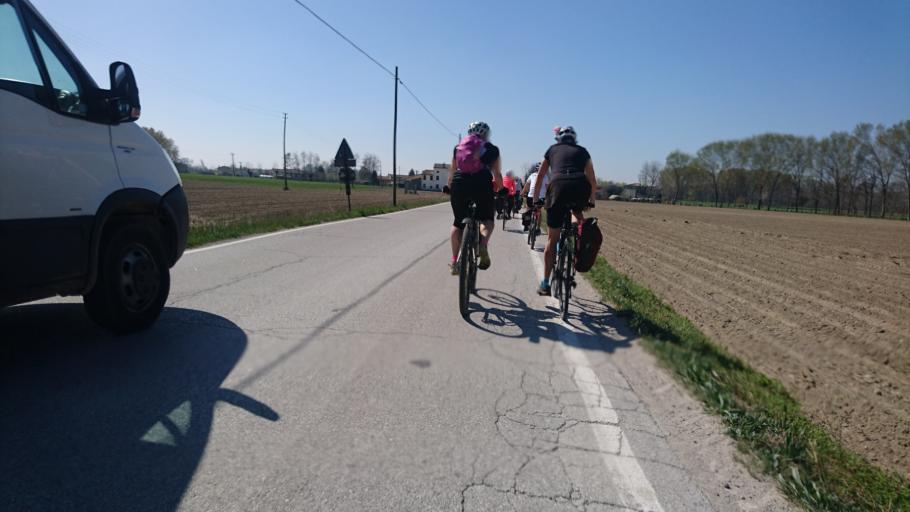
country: IT
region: Veneto
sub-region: Provincia di Padova
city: San Giorgio in Bosco
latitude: 45.5992
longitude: 11.7726
